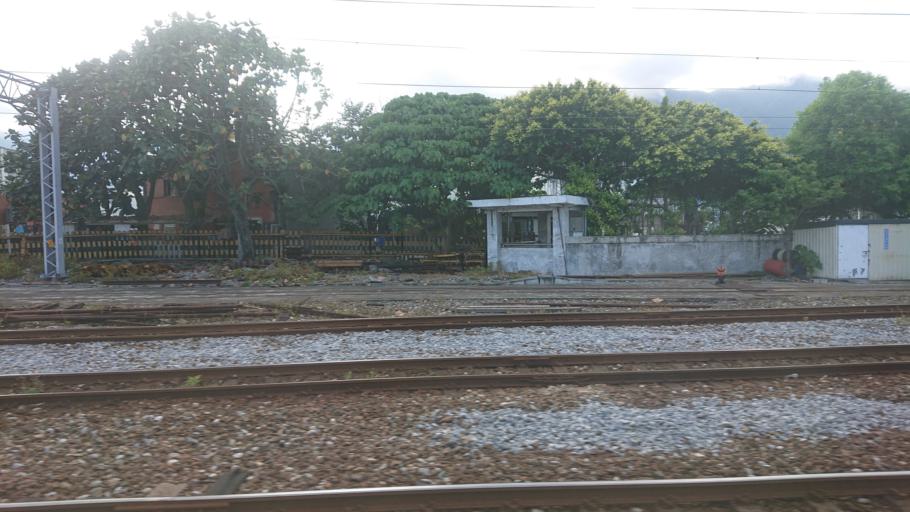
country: TW
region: Taiwan
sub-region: Hualien
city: Hualian
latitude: 23.9898
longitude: 121.5994
